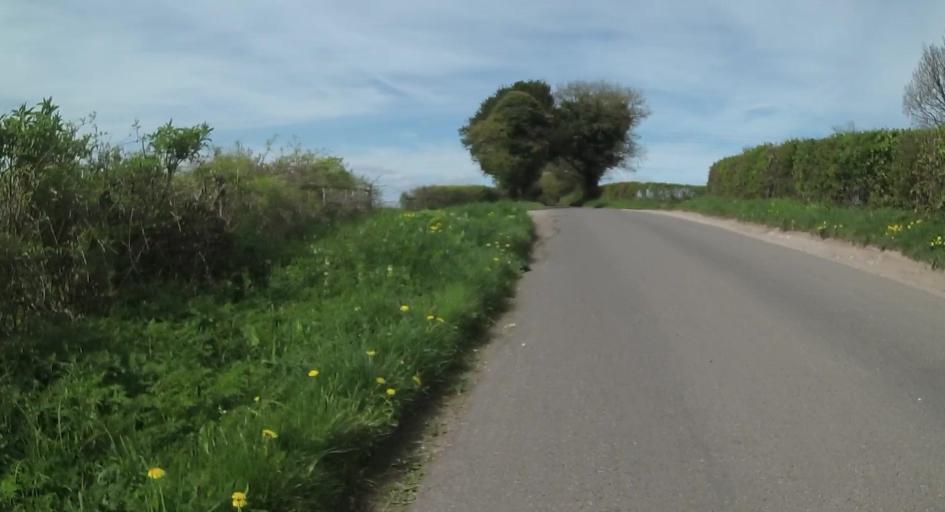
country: GB
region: England
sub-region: Hampshire
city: Winchester
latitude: 51.0597
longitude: -1.3646
